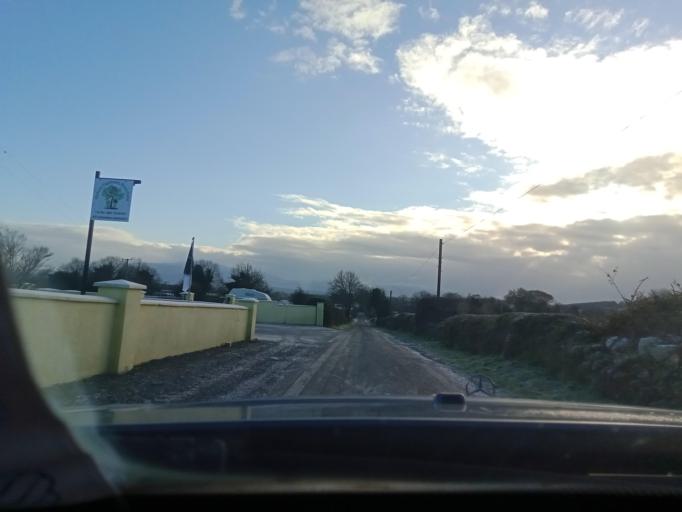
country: IE
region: Leinster
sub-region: Kilkenny
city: Graiguenamanagh
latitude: 52.5968
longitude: -6.9634
